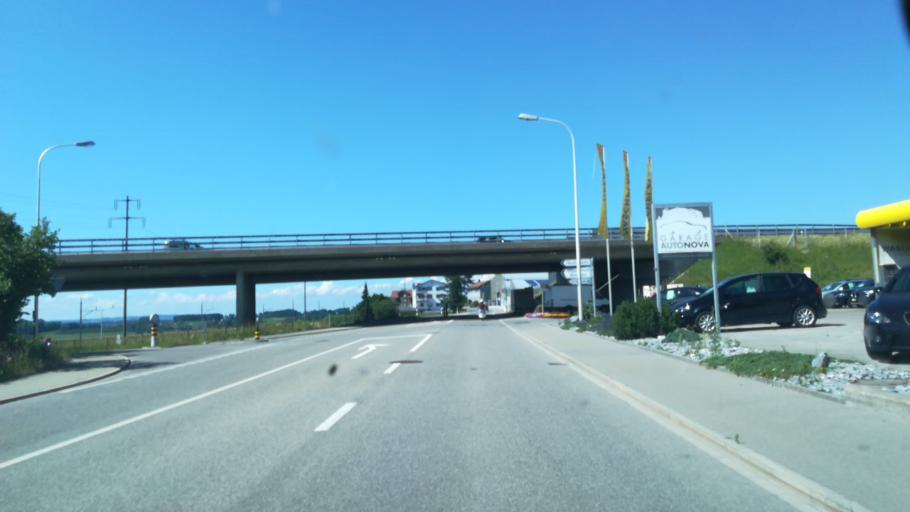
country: CH
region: Saint Gallen
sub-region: Wahlkreis St. Gallen
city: Gossau
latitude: 47.4246
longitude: 9.2410
